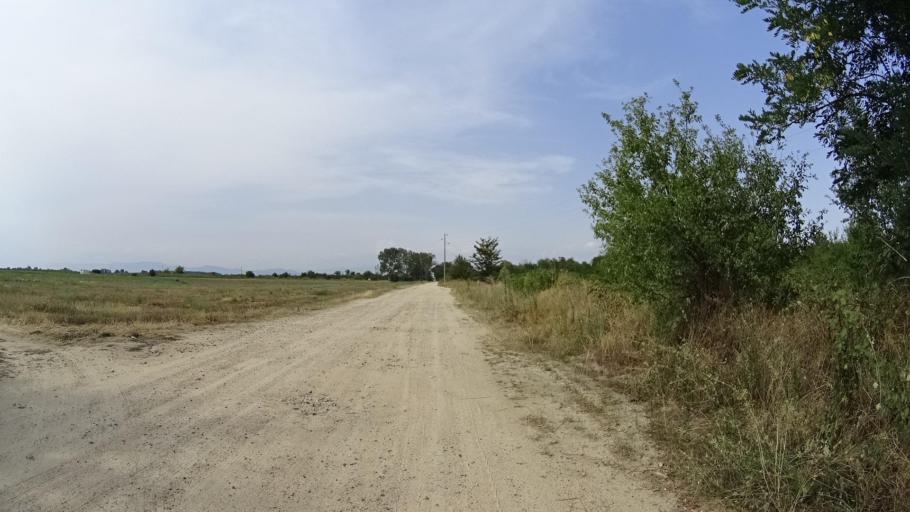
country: BG
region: Plovdiv
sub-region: Obshtina Kaloyanovo
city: Kaloyanovo
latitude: 42.3022
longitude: 24.7991
